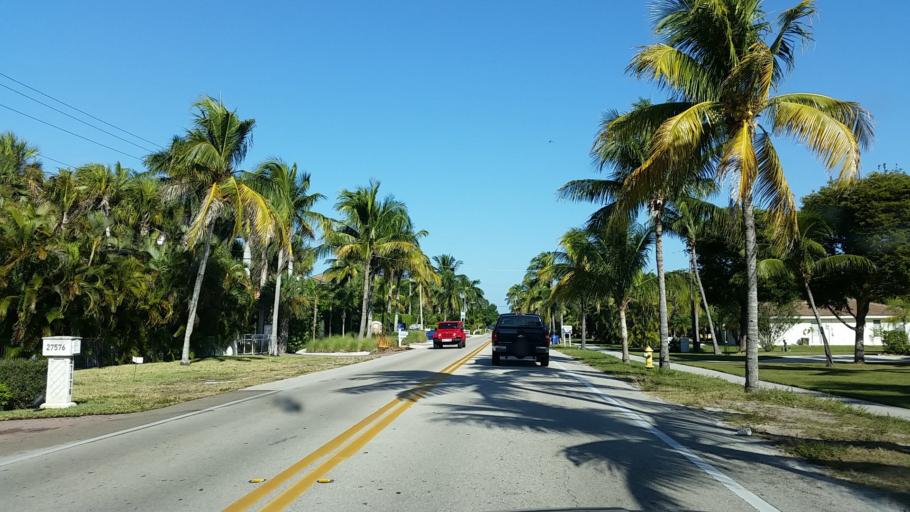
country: US
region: Florida
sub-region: Lee County
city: Bonita Springs
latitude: 26.3372
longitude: -81.8477
